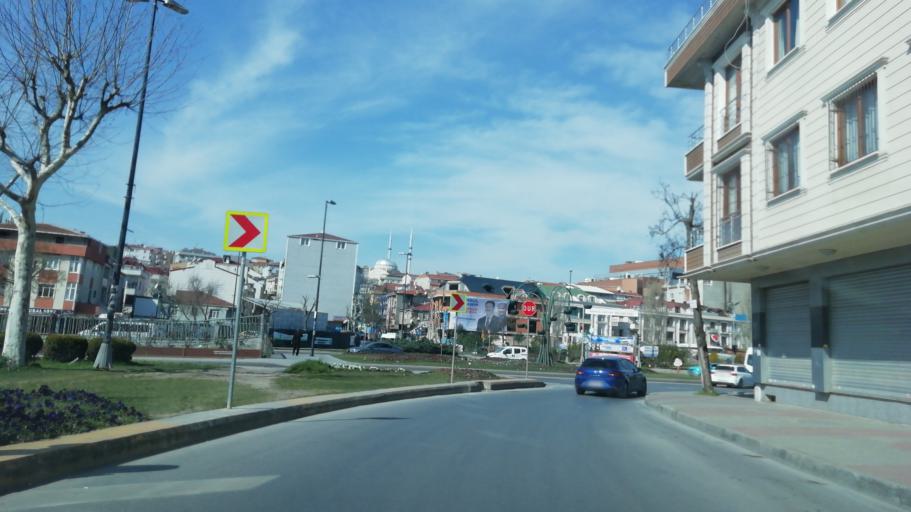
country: TR
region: Istanbul
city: Bahcelievler
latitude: 41.0166
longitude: 28.8492
